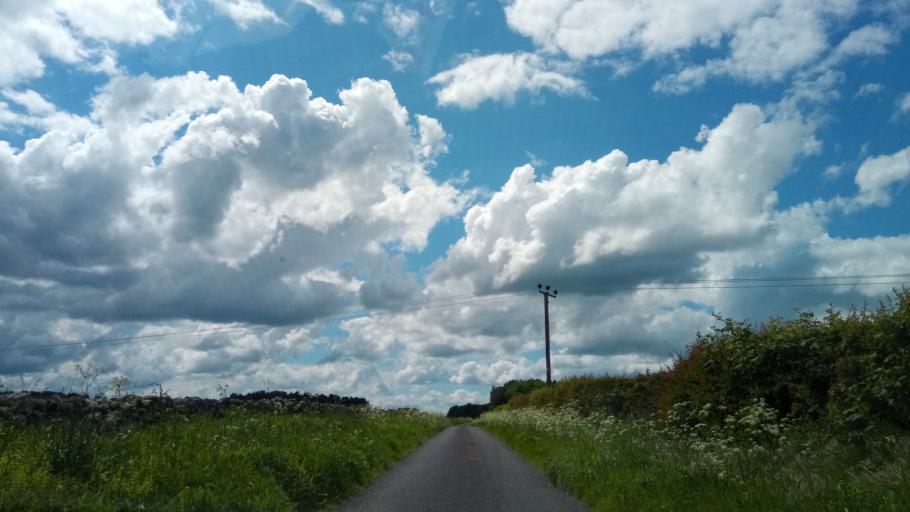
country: GB
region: Scotland
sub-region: The Scottish Borders
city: Coldstream
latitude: 55.6016
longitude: -2.2703
